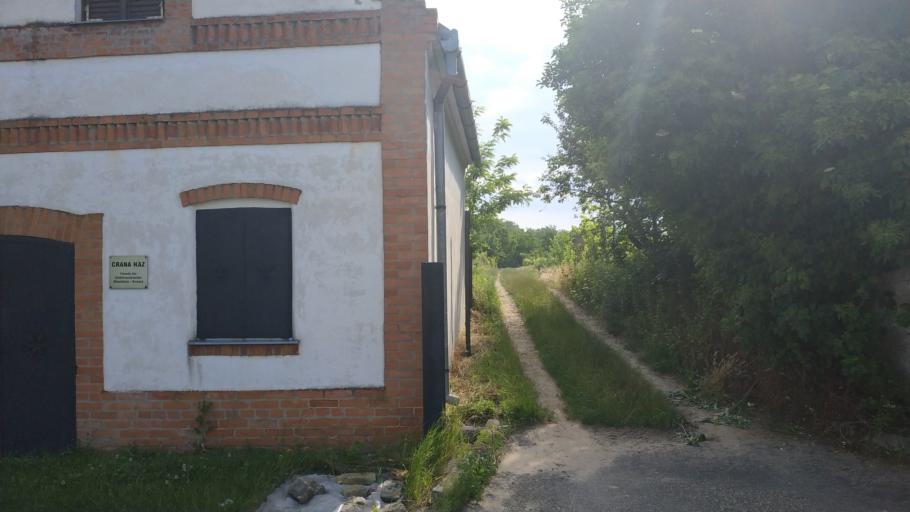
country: HU
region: Bacs-Kiskun
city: Hajos
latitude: 46.3865
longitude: 19.1531
